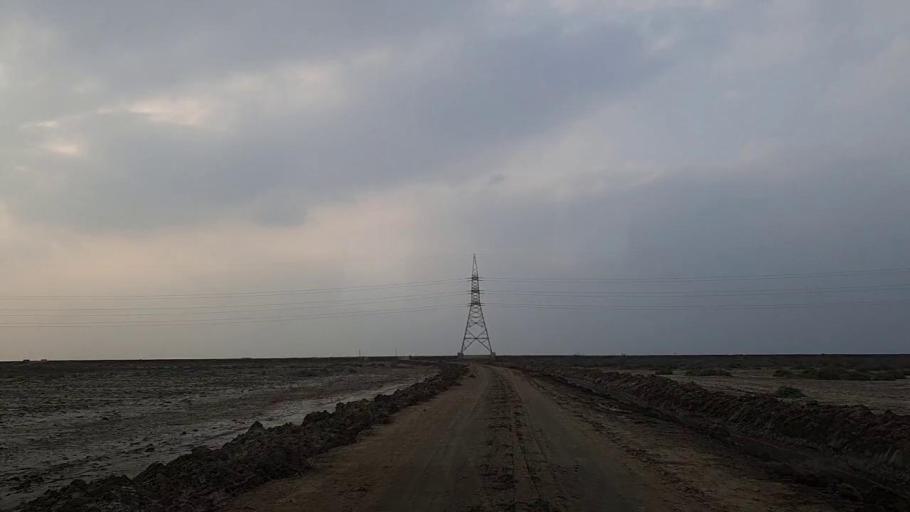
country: PK
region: Sindh
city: Gharo
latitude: 24.6280
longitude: 67.4997
